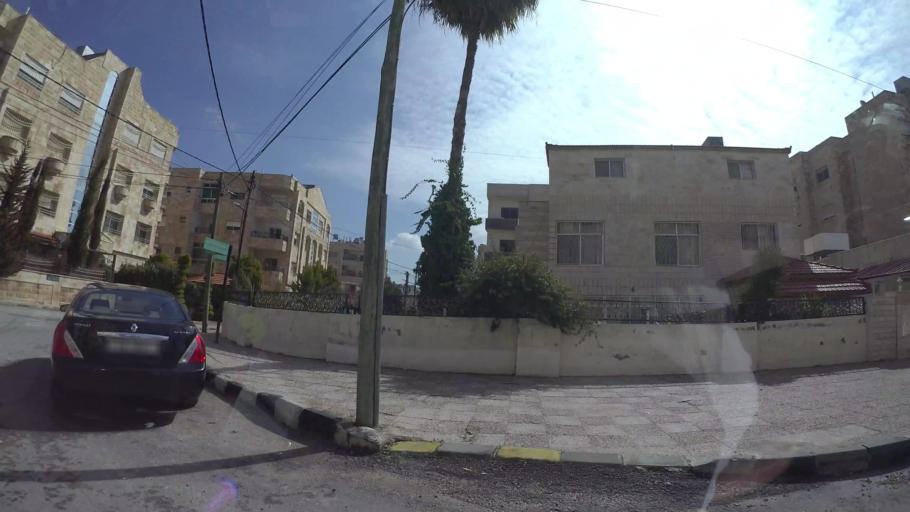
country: JO
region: Amman
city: Al Jubayhah
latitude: 31.9941
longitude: 35.9007
